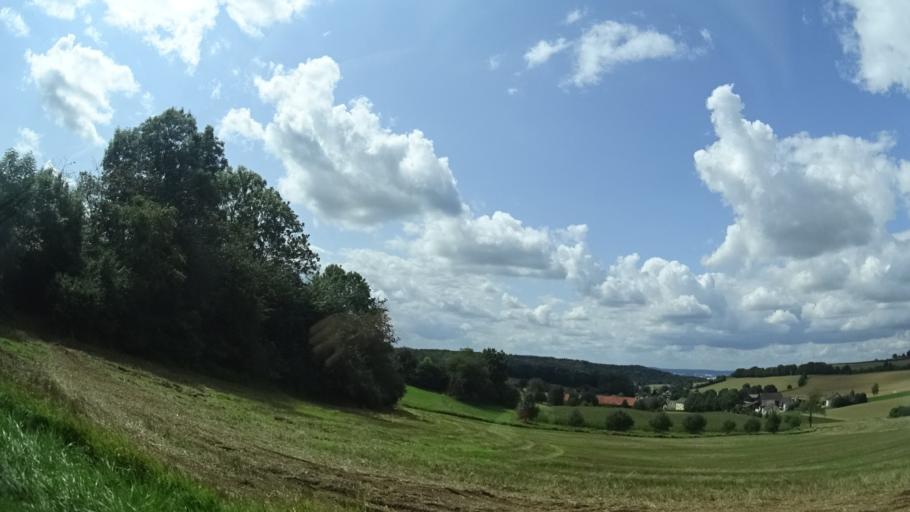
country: DE
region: Bavaria
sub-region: Upper Franconia
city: Neustadt bei Coburg
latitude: 50.2880
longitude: 11.0932
